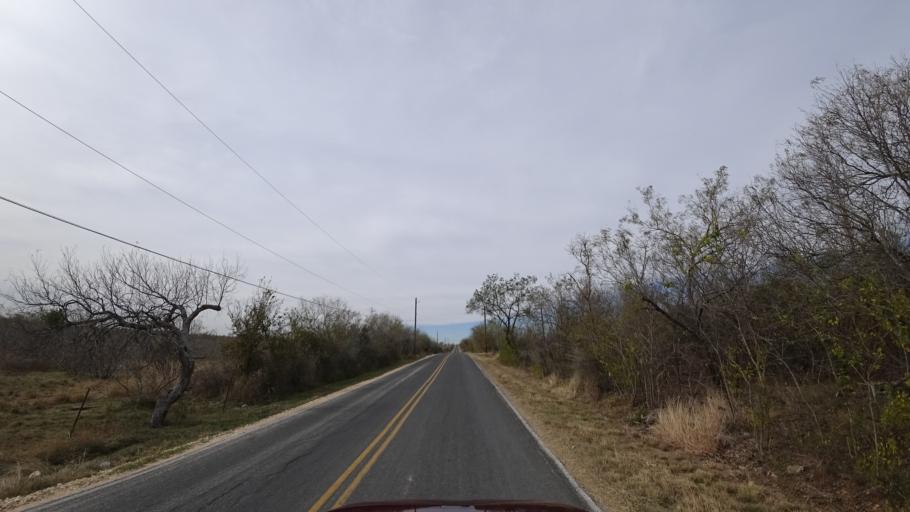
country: US
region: Texas
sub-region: Travis County
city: Garfield
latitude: 30.1374
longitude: -97.6068
